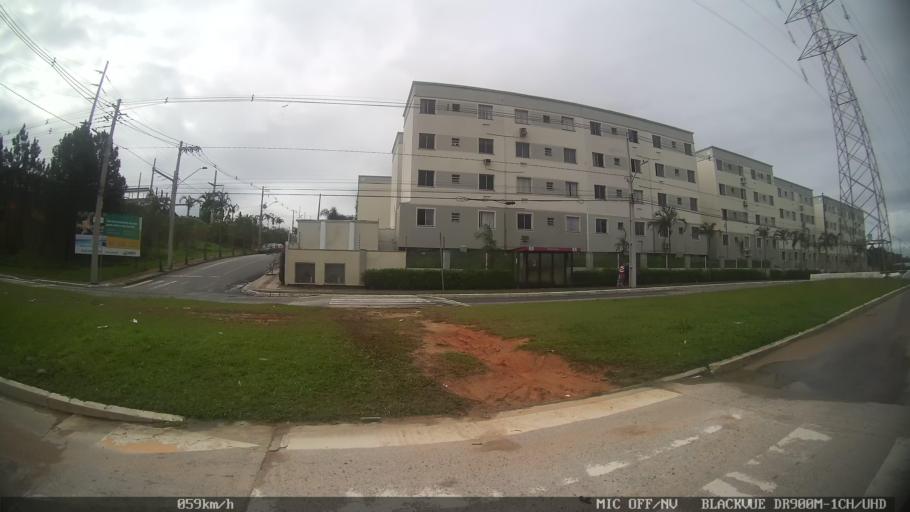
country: BR
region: Santa Catarina
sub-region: Sao Jose
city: Campinas
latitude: -27.5571
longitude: -48.6410
